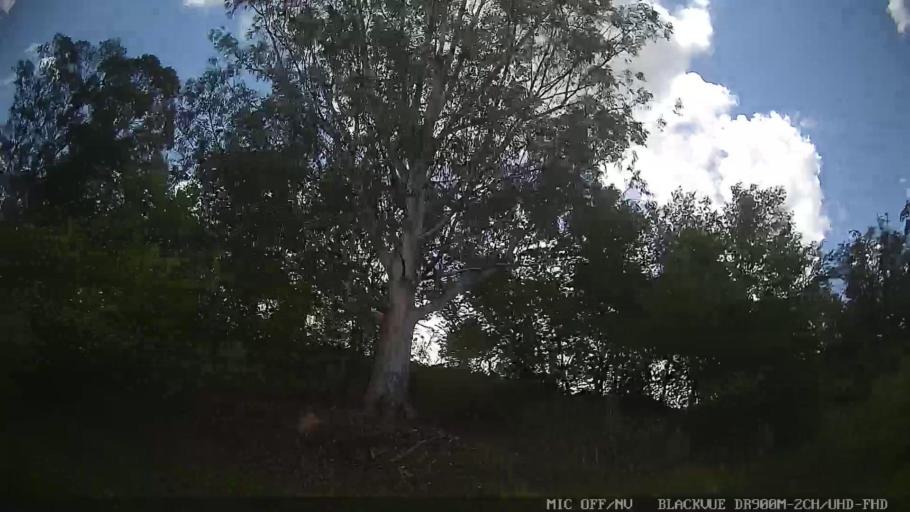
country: BR
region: Sao Paulo
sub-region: Serra Negra
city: Serra Negra
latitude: -22.6475
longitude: -46.7375
